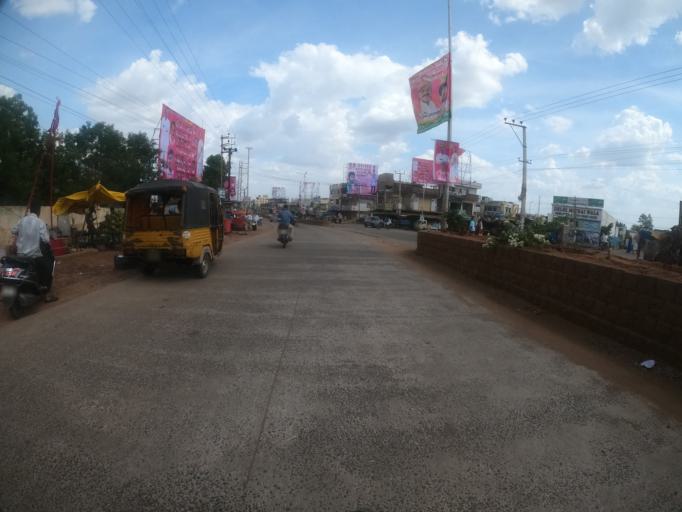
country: IN
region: Telangana
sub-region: Rangareddi
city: Sriramnagar
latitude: 17.3137
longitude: 78.1393
